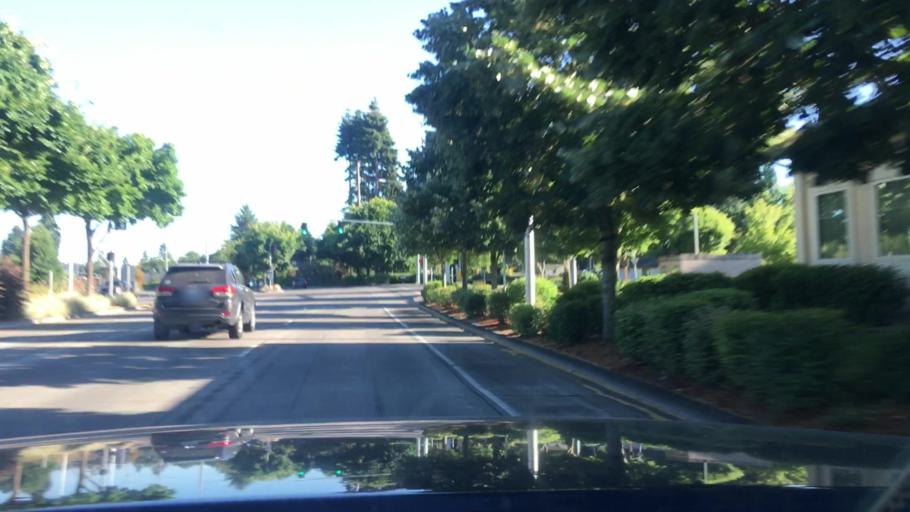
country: US
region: Oregon
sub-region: Lane County
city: Springfield
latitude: 44.0785
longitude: -123.0311
